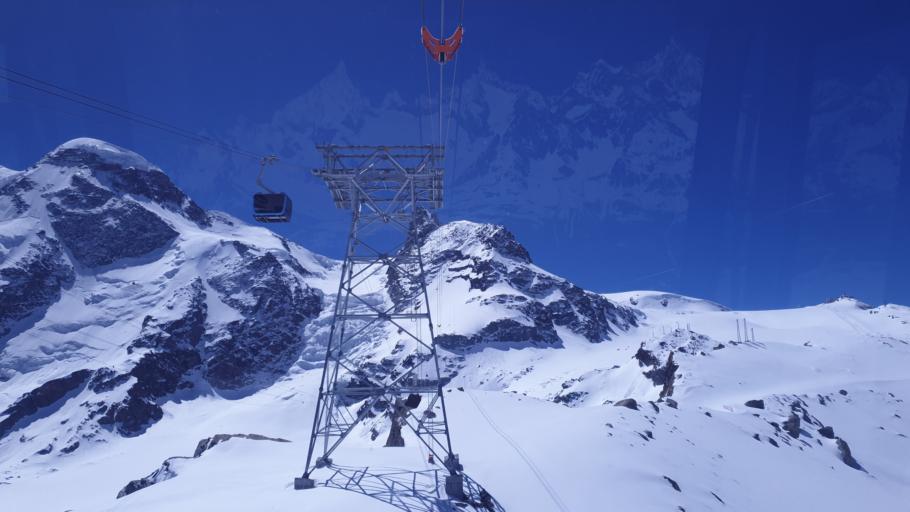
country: CH
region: Valais
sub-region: Visp District
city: Zermatt
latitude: 45.9639
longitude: 7.7231
